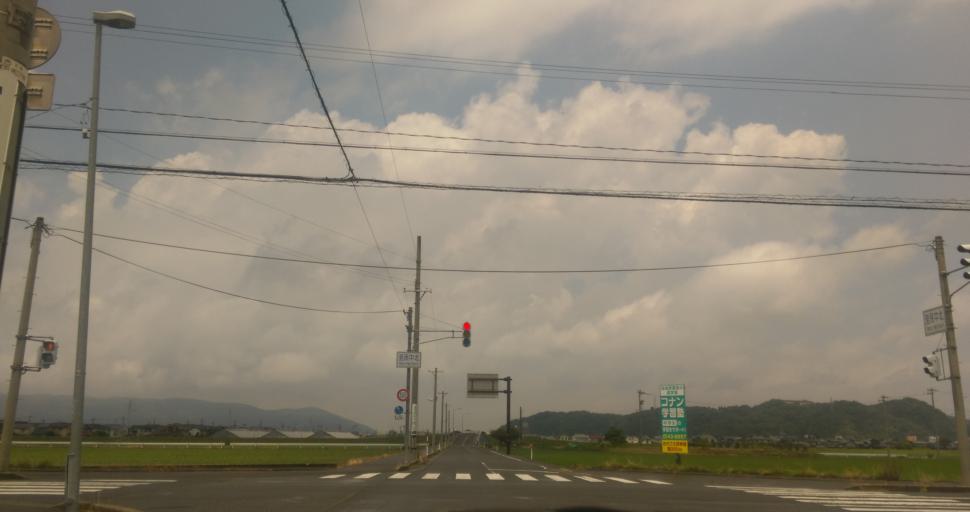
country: JP
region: Fukui
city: Fukui-shi
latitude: 36.0297
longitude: 136.1879
